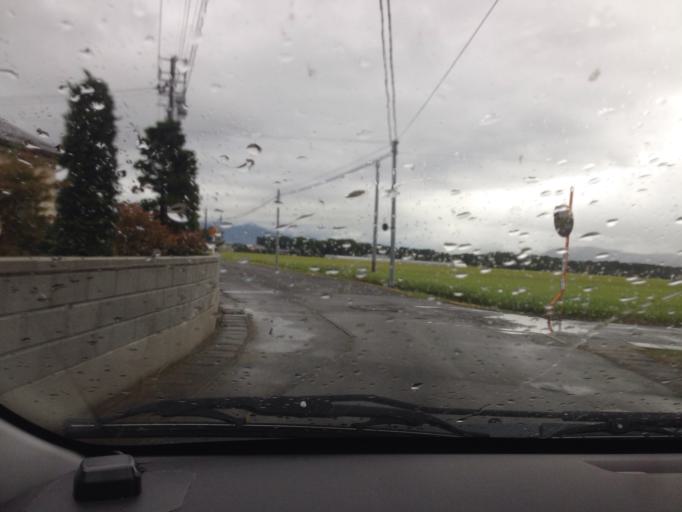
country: JP
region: Fukushima
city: Inawashiro
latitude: 37.4121
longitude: 140.1263
